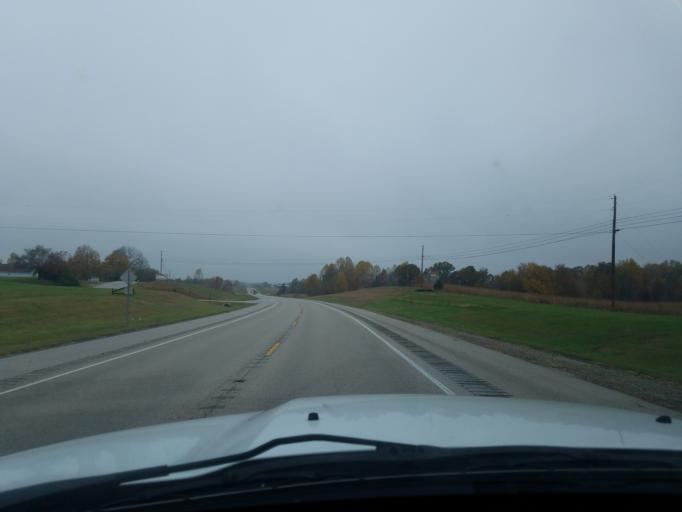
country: US
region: Kentucky
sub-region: Green County
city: Greensburg
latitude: 37.4119
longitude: -85.4896
